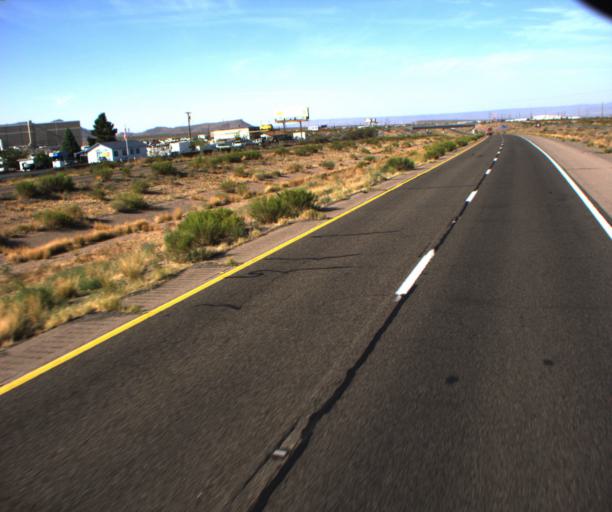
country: US
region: Arizona
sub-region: Mohave County
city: Kingman
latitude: 35.1523
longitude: -114.0906
